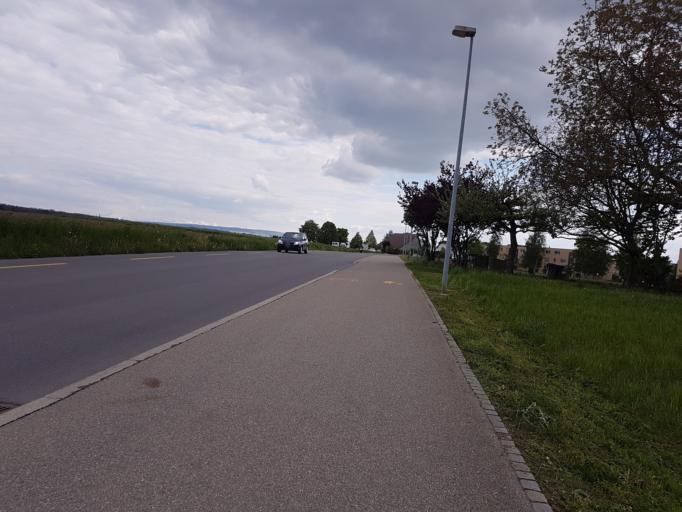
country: CH
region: Bern
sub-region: Biel/Bienne District
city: Orpund
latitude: 47.1429
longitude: 7.3158
